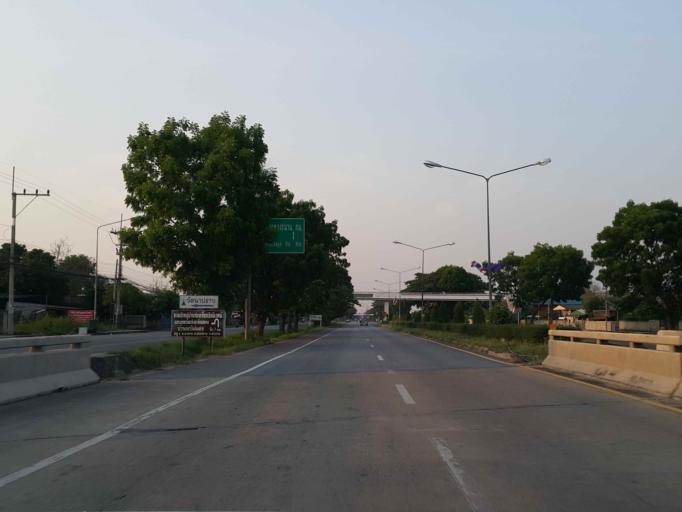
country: TH
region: Lampang
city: Sop Prap
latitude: 17.8838
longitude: 99.3383
